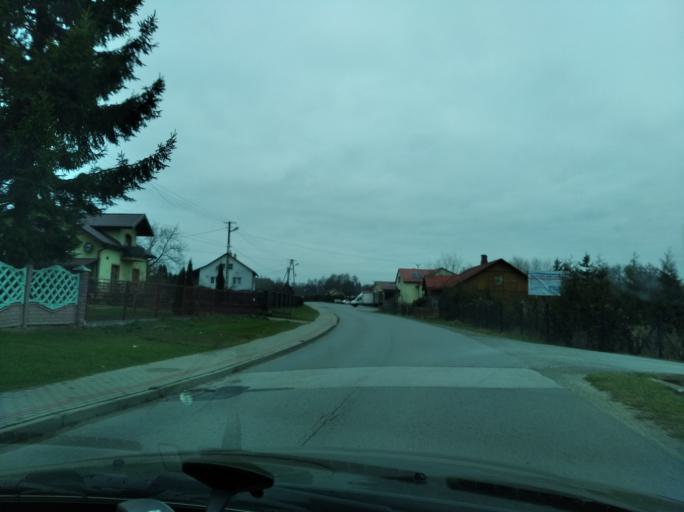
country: PL
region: Subcarpathian Voivodeship
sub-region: Powiat lancucki
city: Rakszawa
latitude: 50.1734
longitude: 22.2351
